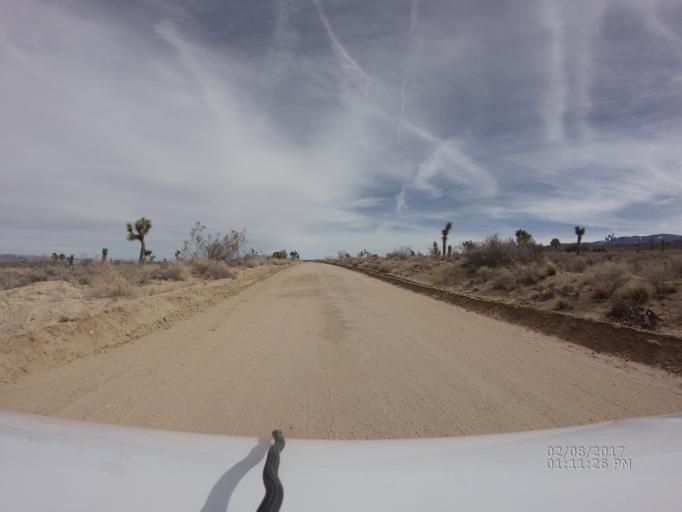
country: US
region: California
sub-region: Los Angeles County
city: Lake Los Angeles
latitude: 34.4754
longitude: -117.8025
